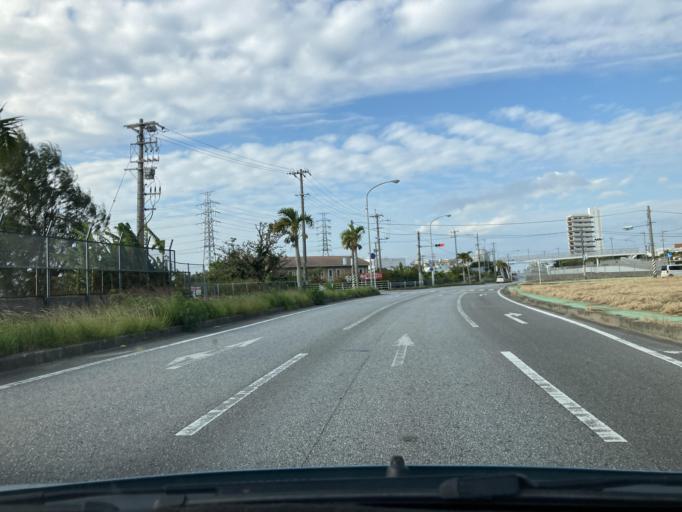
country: JP
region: Okinawa
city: Okinawa
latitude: 26.3195
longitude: 127.7895
